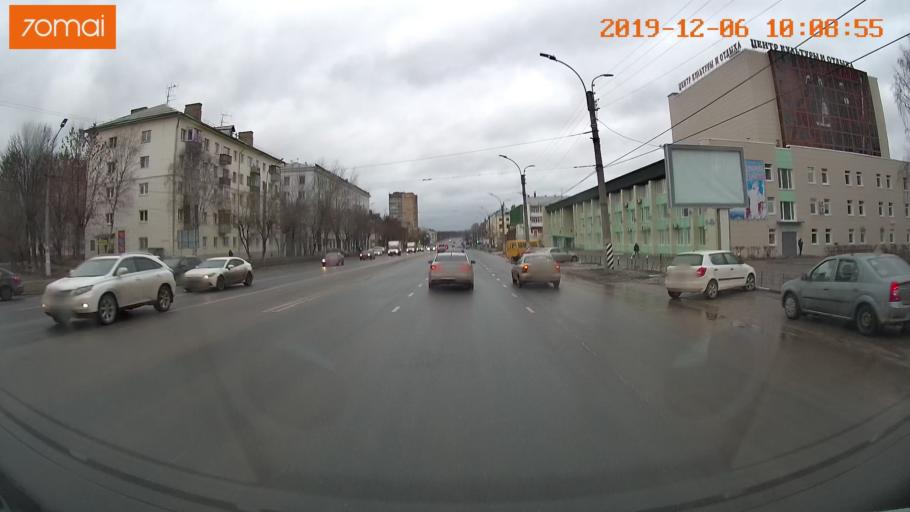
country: RU
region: Ivanovo
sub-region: Gorod Ivanovo
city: Ivanovo
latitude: 57.0189
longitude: 40.9689
